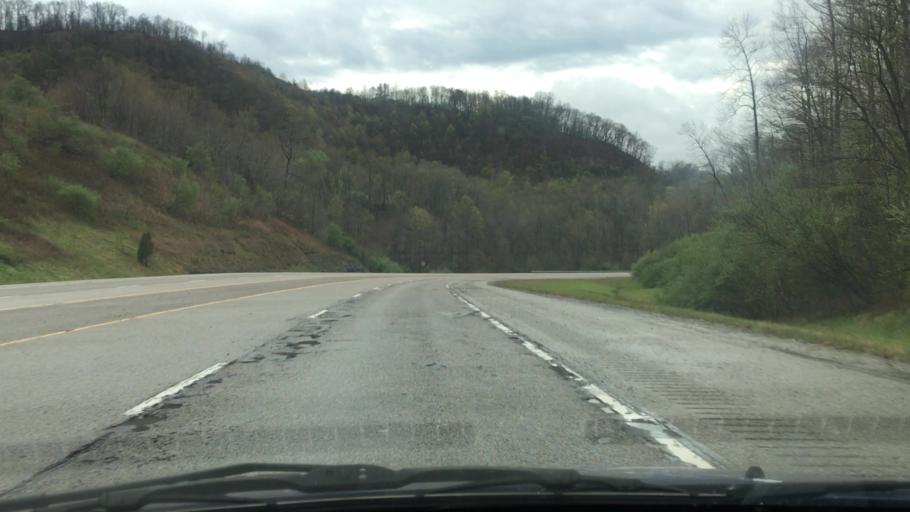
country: US
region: Kentucky
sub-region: Letcher County
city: Jenkins
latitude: 37.2129
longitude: -82.6246
